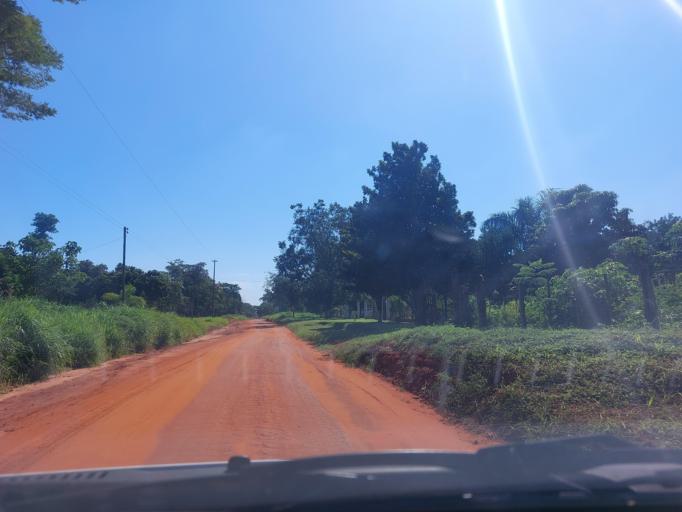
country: PY
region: San Pedro
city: Lima
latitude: -24.1515
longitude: -56.0114
